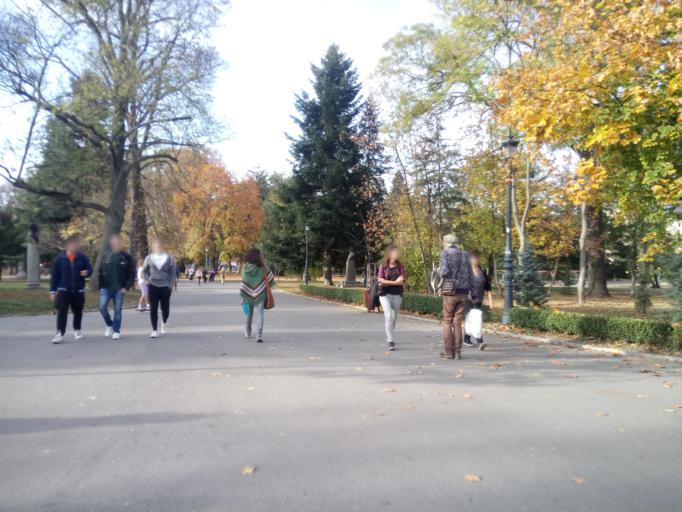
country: BG
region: Sofia-Capital
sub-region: Stolichna Obshtina
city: Sofia
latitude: 42.6879
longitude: 23.3396
